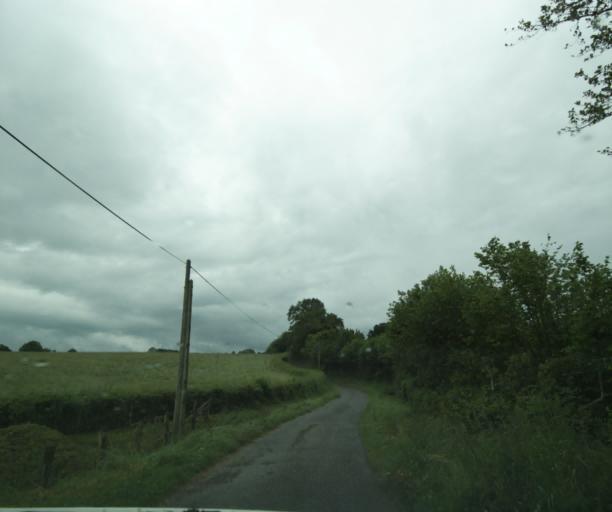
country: FR
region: Bourgogne
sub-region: Departement de Saone-et-Loire
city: Palinges
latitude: 46.5342
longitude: 4.2736
